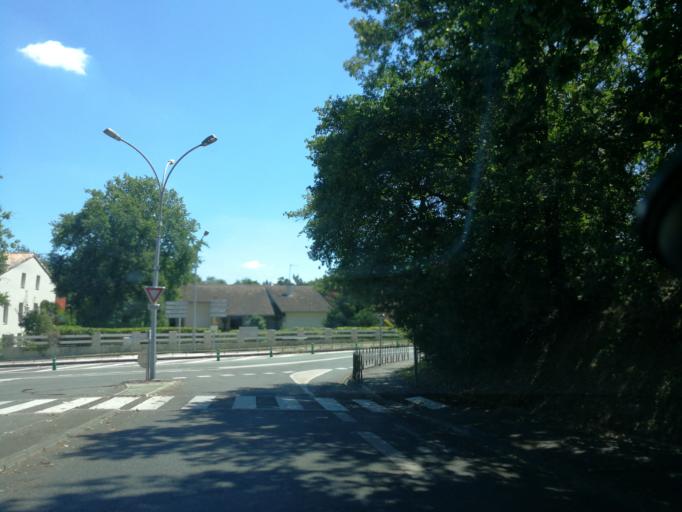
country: FR
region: Midi-Pyrenees
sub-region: Departement de la Haute-Garonne
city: Balma
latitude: 43.6020
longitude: 1.5073
